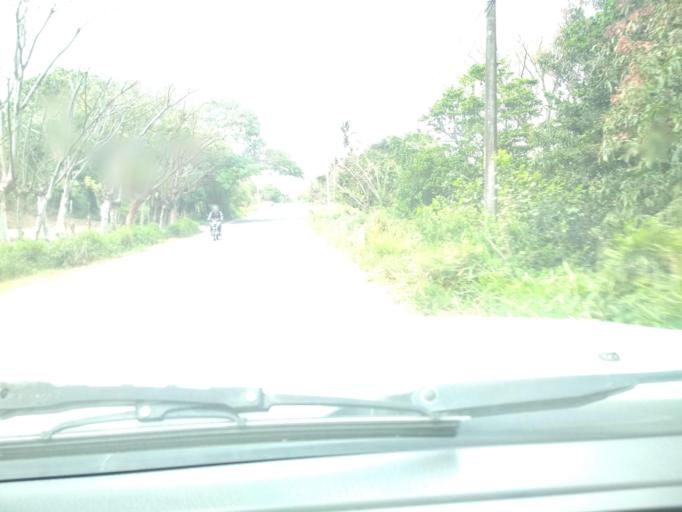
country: MX
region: Veracruz
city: Anton Lizardo
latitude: 19.0429
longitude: -95.9861
